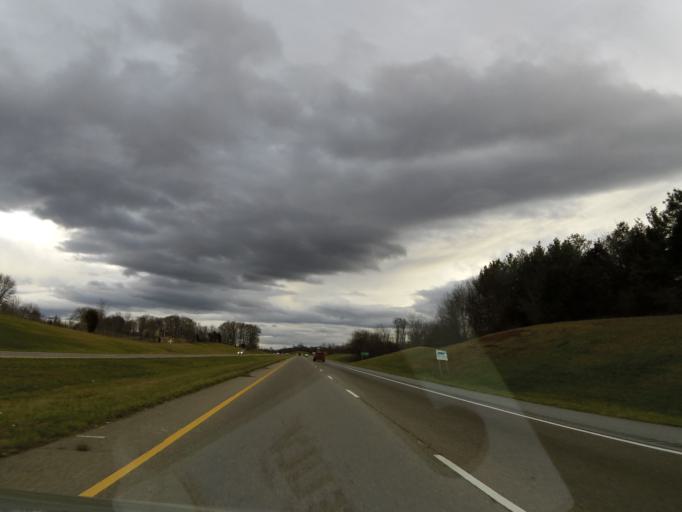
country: US
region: Tennessee
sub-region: Carter County
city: Pine Crest
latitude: 36.3130
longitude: -82.3203
